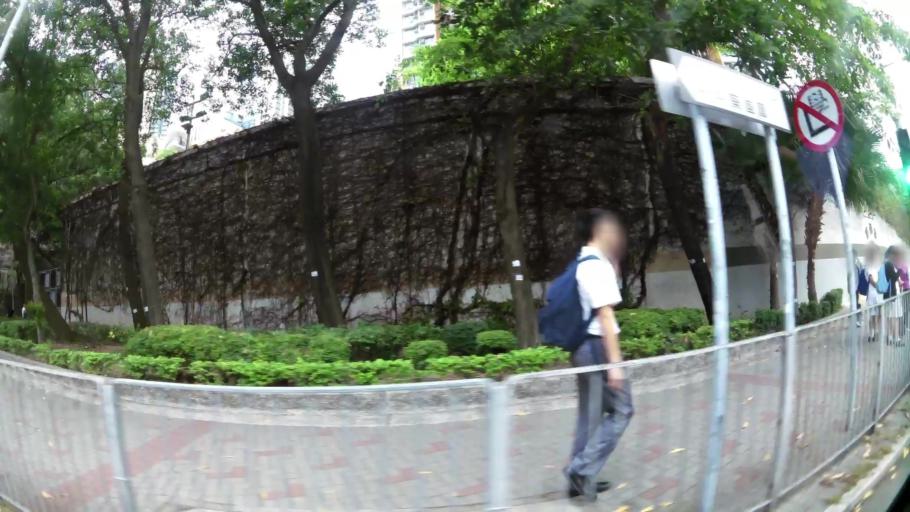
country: HK
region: Tsuen Wan
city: Tsuen Wan
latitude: 22.3659
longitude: 114.1306
